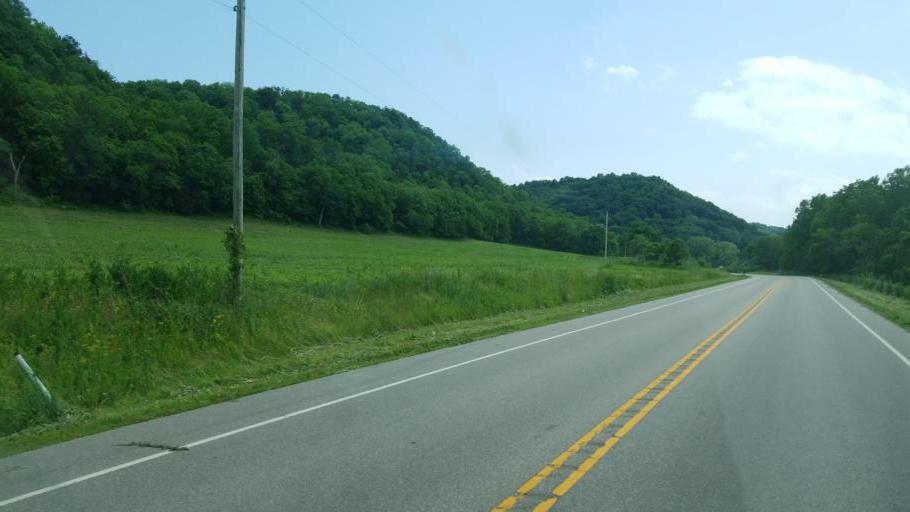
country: US
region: Wisconsin
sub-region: Vernon County
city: Viroqua
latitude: 43.4794
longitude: -90.6917
